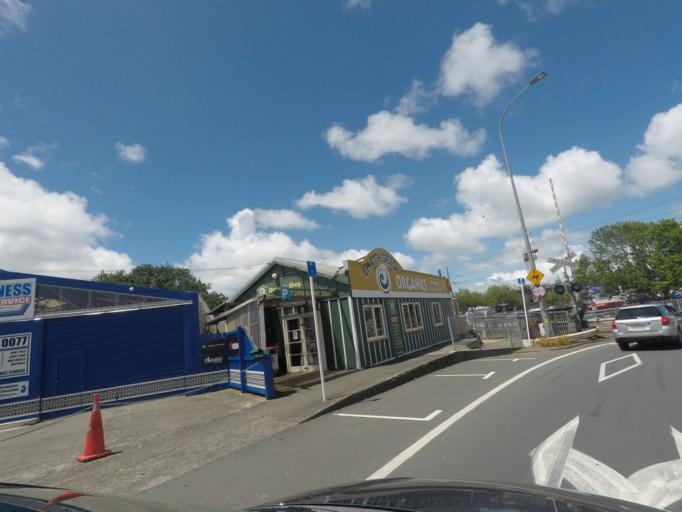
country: NZ
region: Auckland
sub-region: Auckland
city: Waitakere
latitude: -36.9097
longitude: 174.6523
